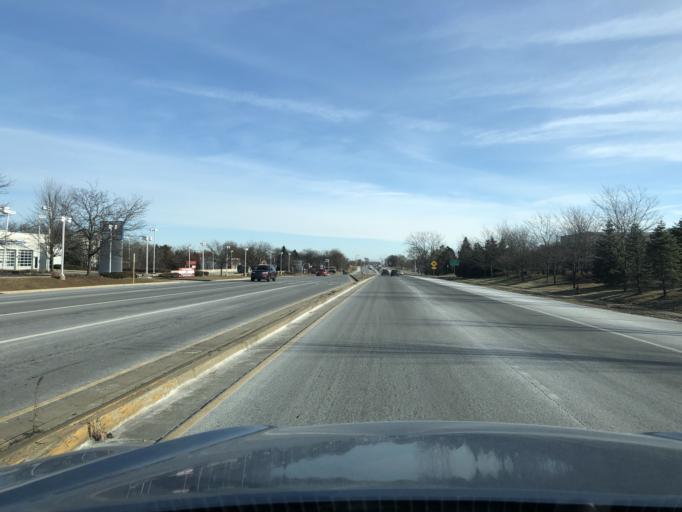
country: US
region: Illinois
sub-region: Lake County
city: Grandwood Park
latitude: 42.3859
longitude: -87.9951
